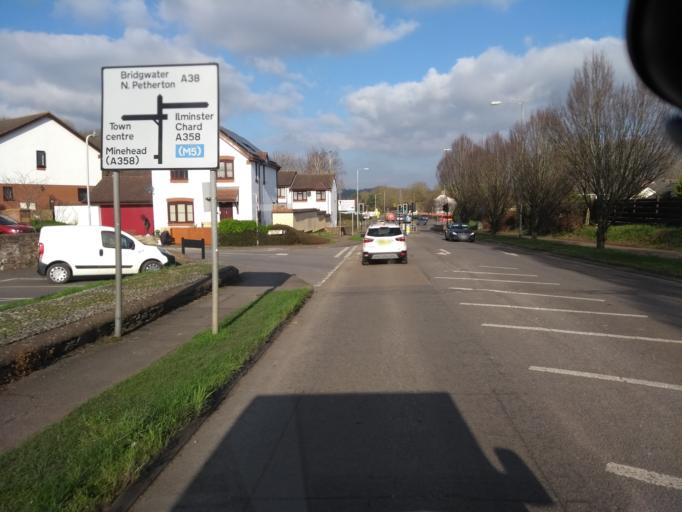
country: GB
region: England
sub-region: Somerset
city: Taunton
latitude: 51.0229
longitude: -3.0719
